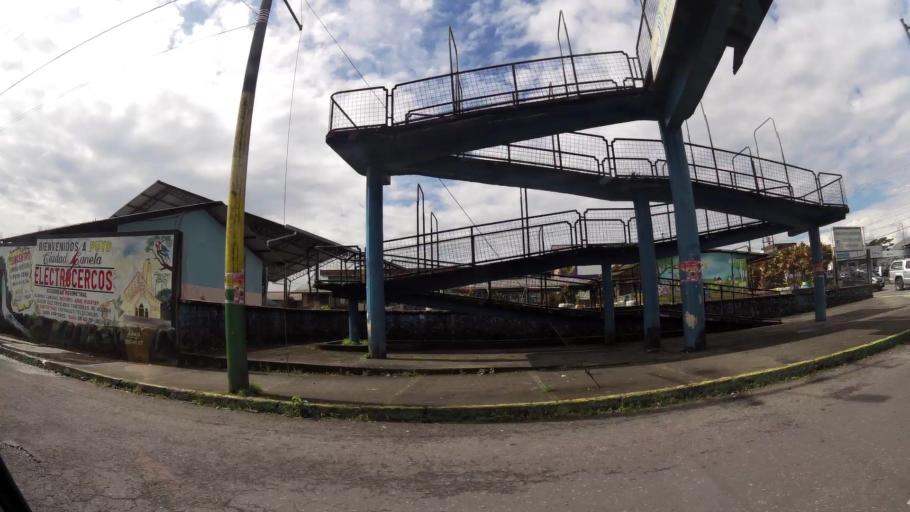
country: EC
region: Pastaza
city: Puyo
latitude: -1.4930
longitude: -77.9996
